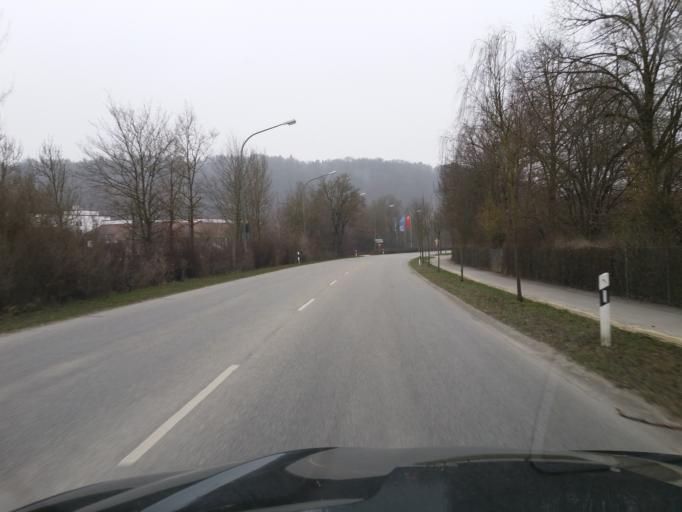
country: DE
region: Bavaria
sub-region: Lower Bavaria
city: Stallwang
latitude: 48.5585
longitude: 12.2009
